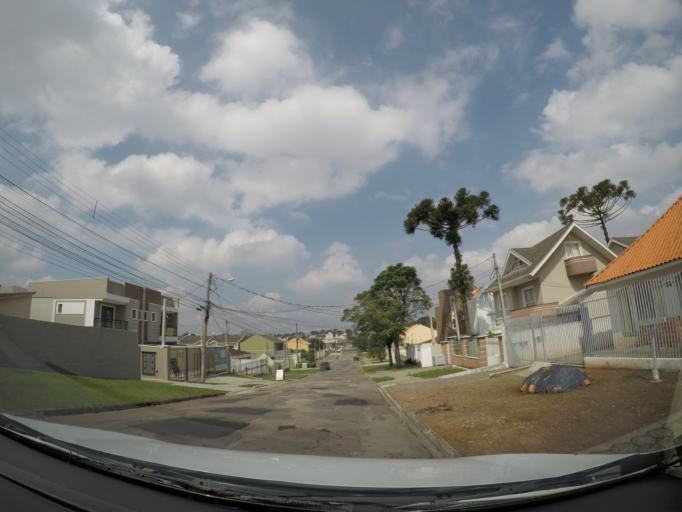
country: BR
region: Parana
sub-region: Curitiba
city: Curitiba
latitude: -25.4868
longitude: -49.2534
